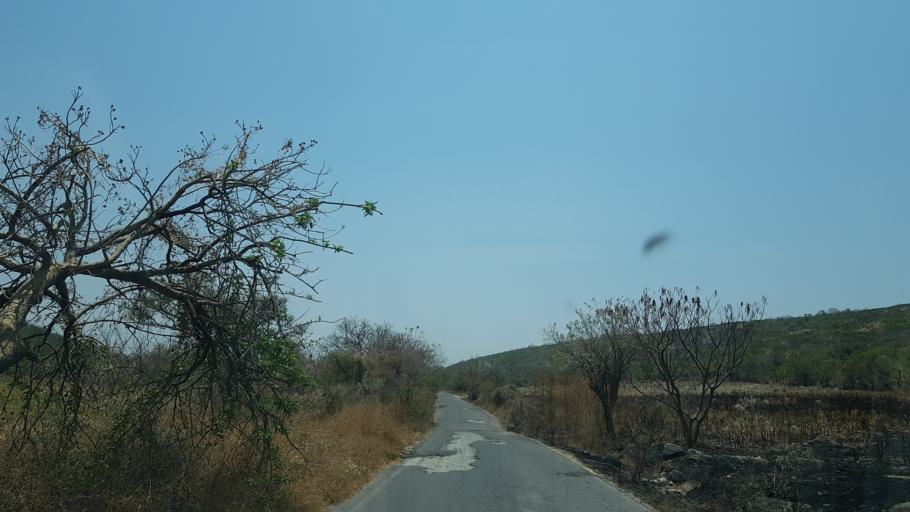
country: MX
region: Puebla
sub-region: Atzitzihuacan
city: San Miguel Aguacomulican
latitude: 18.7983
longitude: -98.5466
